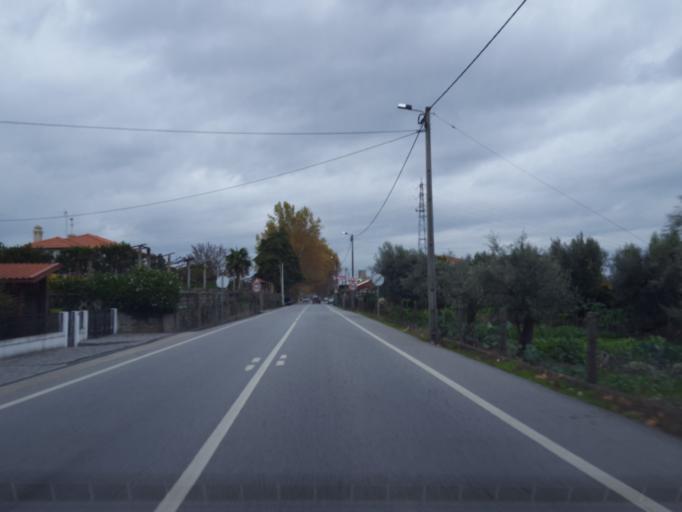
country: PT
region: Porto
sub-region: Marco de Canaveses
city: Marco de Canavezes
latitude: 41.1707
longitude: -8.1511
